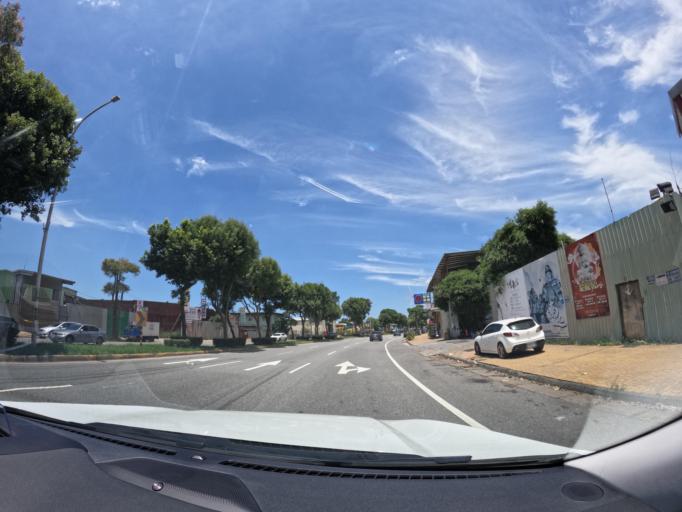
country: TW
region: Taiwan
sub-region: Taoyuan
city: Taoyuan
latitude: 25.0599
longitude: 121.3537
